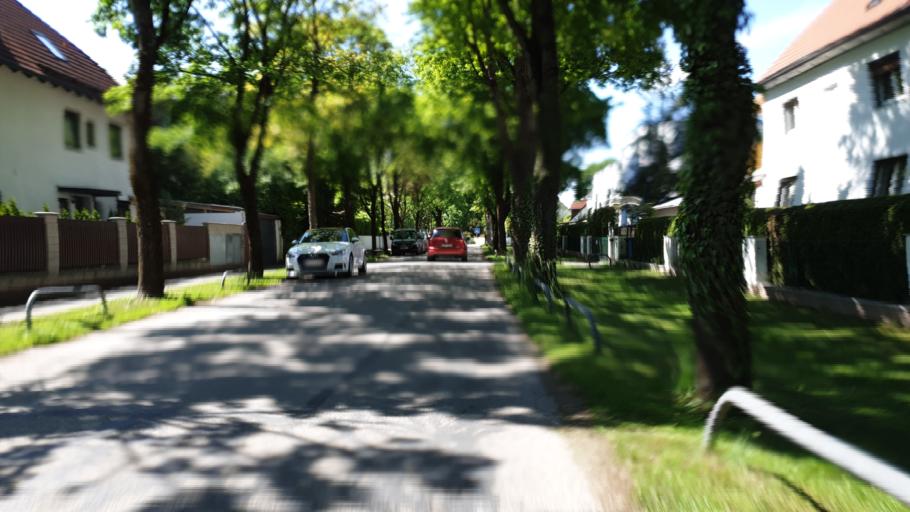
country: DE
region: Bavaria
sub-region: Upper Bavaria
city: Pasing
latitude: 48.1659
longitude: 11.4654
